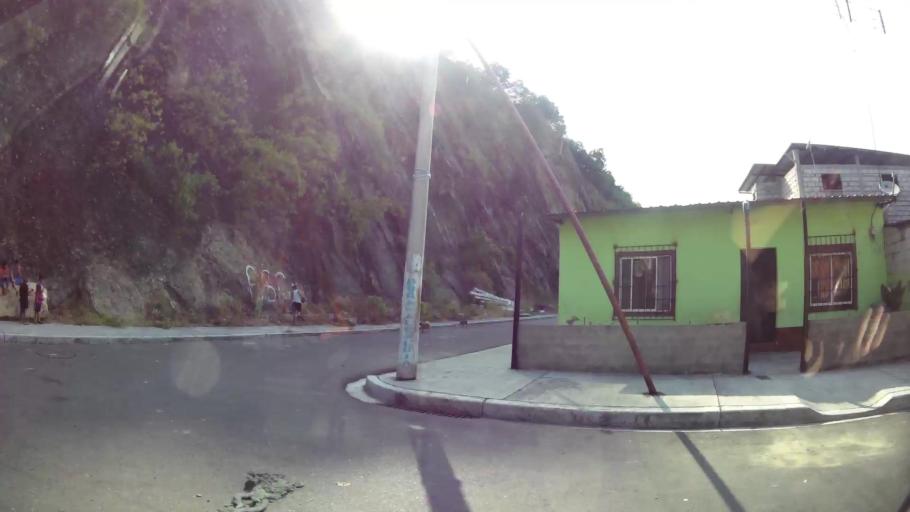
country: EC
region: Guayas
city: Guayaquil
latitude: -2.1864
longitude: -79.9083
